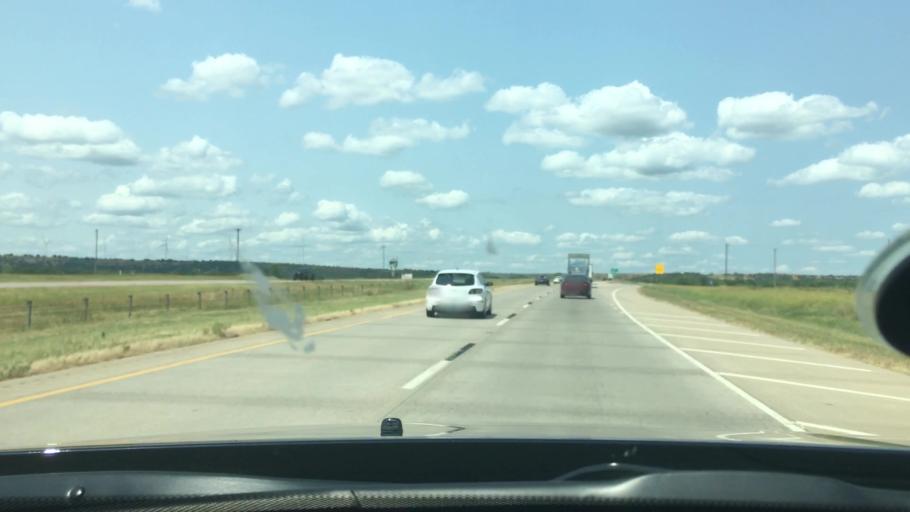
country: US
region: Oklahoma
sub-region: Carter County
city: Ardmore
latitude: 34.3282
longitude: -97.1540
